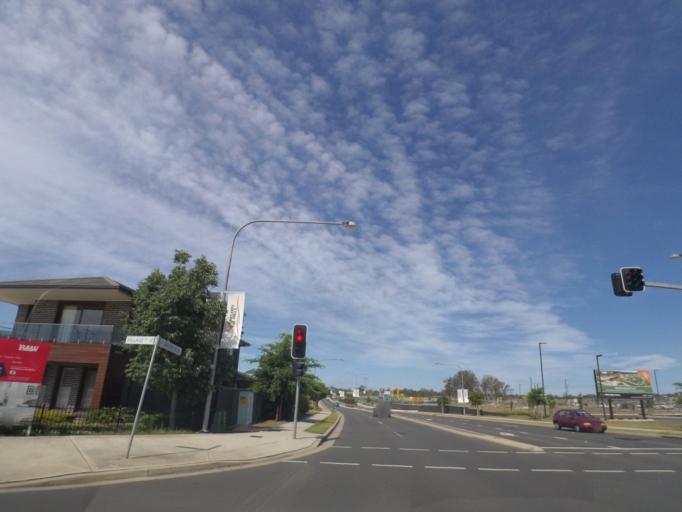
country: AU
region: New South Wales
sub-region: Camden
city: Narellan Vale
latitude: -34.0254
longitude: 150.7764
